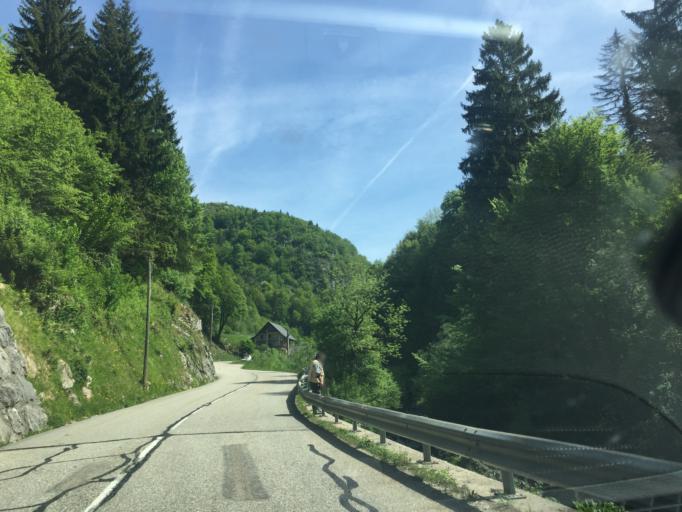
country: FR
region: Rhone-Alpes
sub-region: Departement de l'Isere
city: Saint-Vincent-de-Mercuze
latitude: 45.4305
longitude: 5.8700
